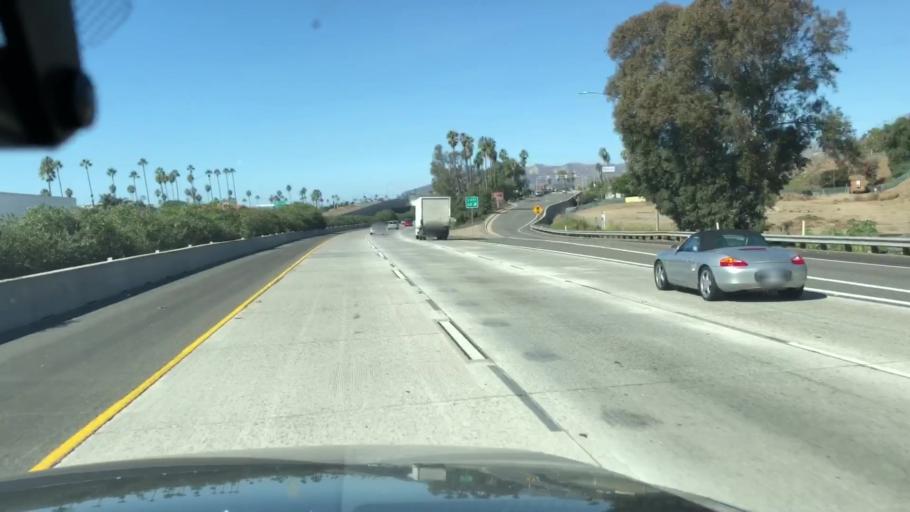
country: US
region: California
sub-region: Ventura County
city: Ventura
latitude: 34.2630
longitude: -119.2654
